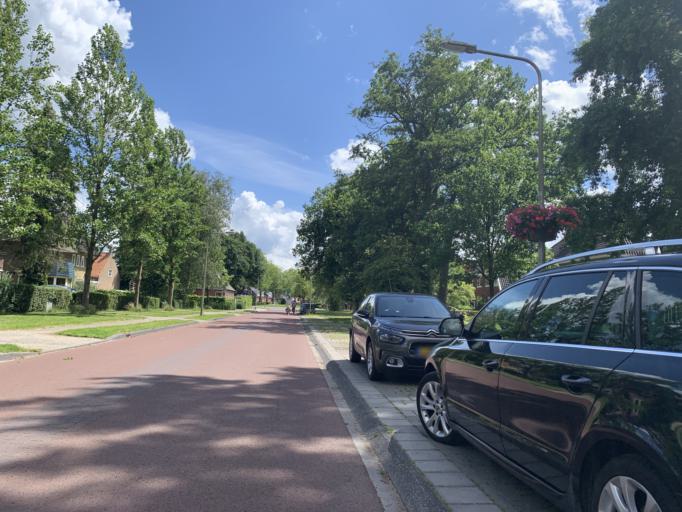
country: NL
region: Groningen
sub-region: Gemeente Haren
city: Haren
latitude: 53.1764
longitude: 6.6067
